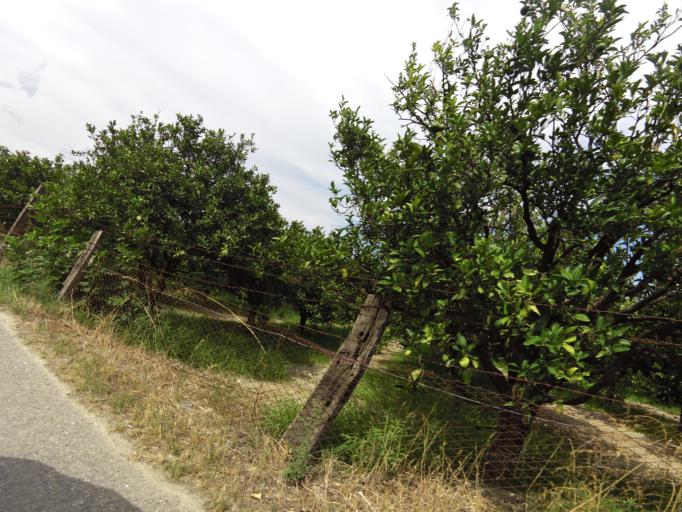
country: IT
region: Calabria
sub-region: Provincia di Reggio Calabria
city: Monasterace
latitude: 38.4552
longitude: 16.5161
